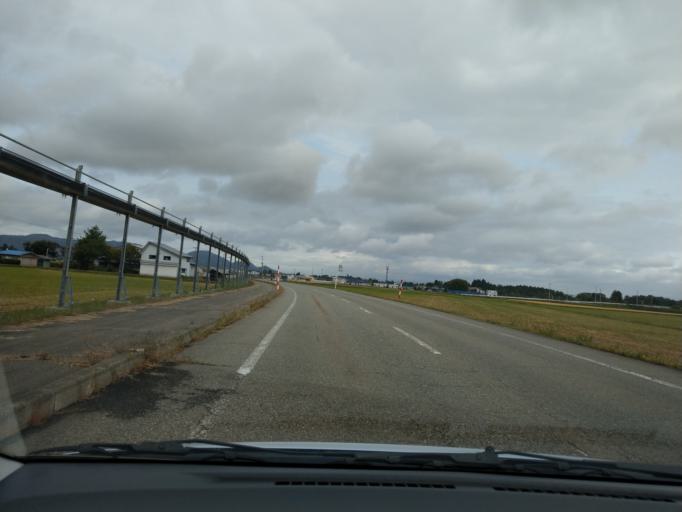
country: JP
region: Akita
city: Omagari
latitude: 39.3932
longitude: 140.4836
